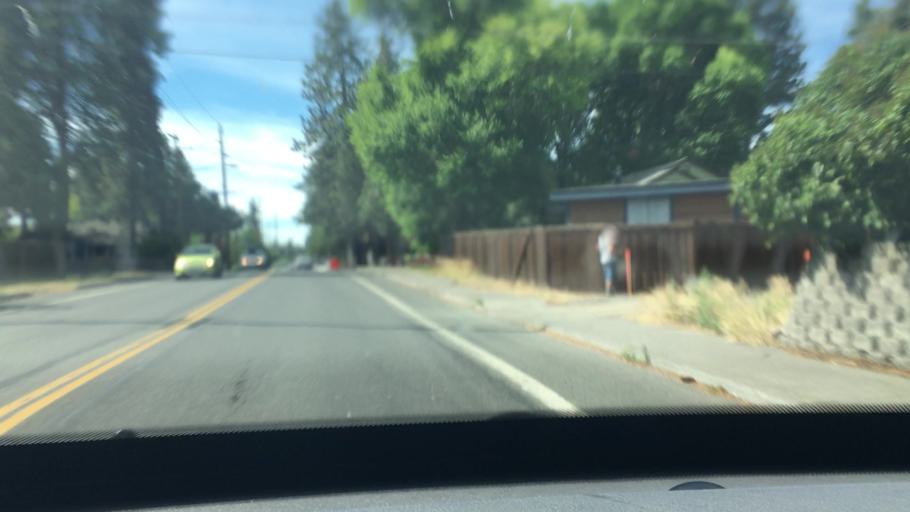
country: US
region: Oregon
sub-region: Deschutes County
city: Bend
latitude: 44.0541
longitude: -121.3319
